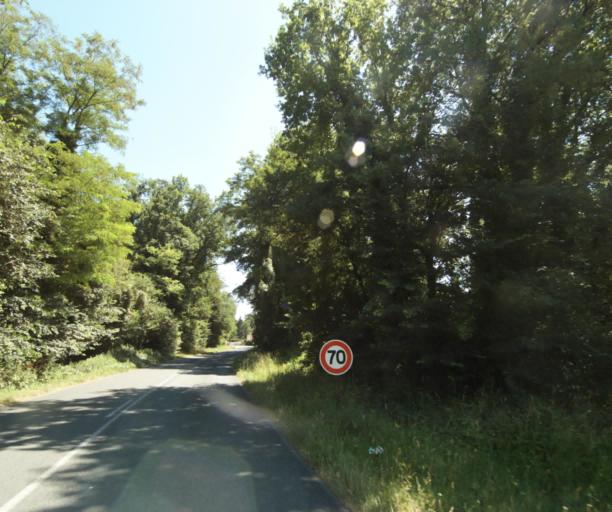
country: FR
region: Ile-de-France
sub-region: Departement de Seine-et-Marne
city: Noisy-sur-Ecole
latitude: 48.3660
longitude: 2.5166
